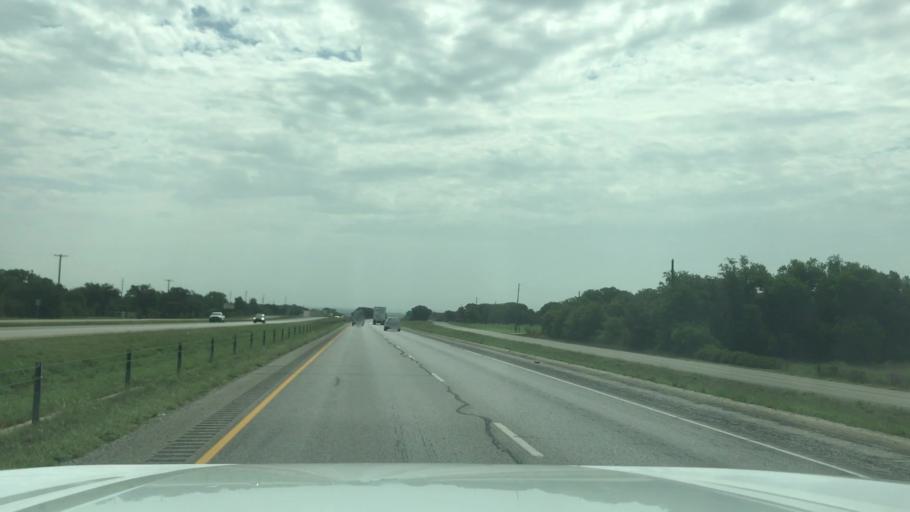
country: US
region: Texas
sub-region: Callahan County
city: Clyde
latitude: 32.4062
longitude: -99.4439
